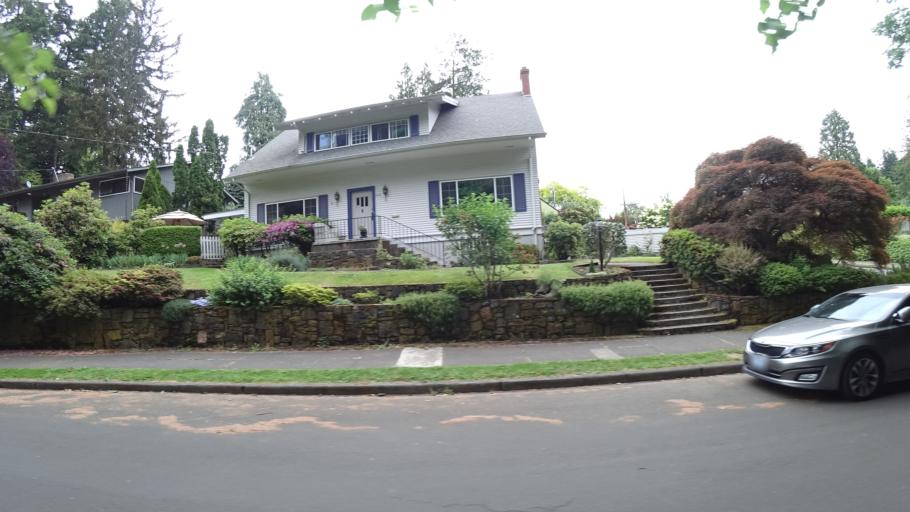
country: US
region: Oregon
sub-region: Multnomah County
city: Lents
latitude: 45.5176
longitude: -122.5942
